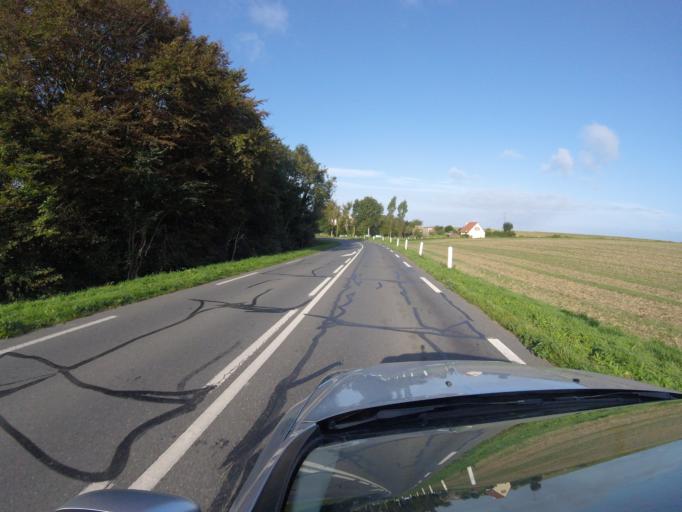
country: FR
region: Haute-Normandie
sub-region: Departement de la Seine-Maritime
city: Fecamp
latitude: 49.7683
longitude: 0.4073
